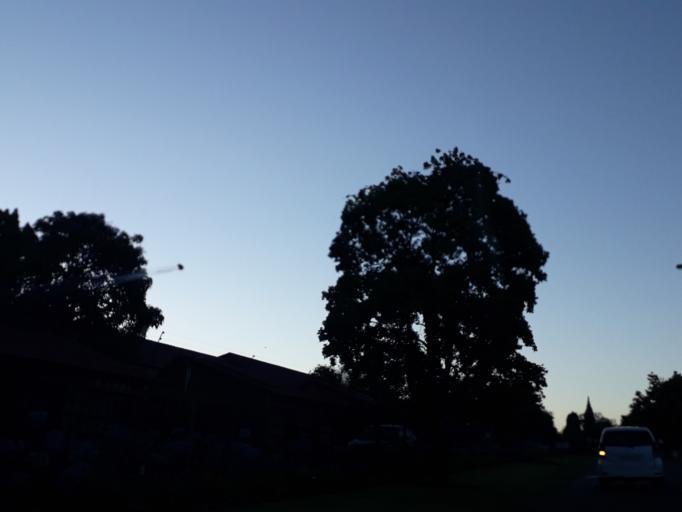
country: ZA
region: Gauteng
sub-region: City of Johannesburg Metropolitan Municipality
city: Roodepoort
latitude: -26.1272
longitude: 27.9482
